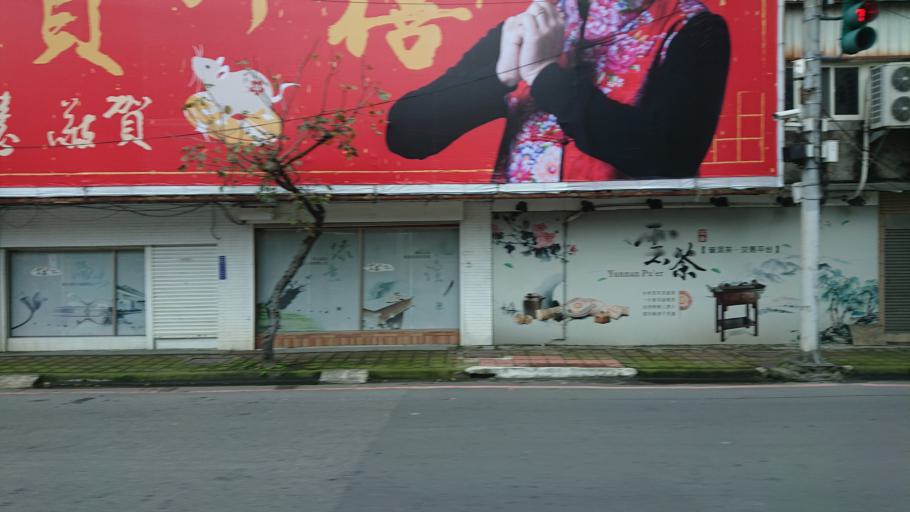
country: TW
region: Taiwan
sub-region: Taoyuan
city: Taoyuan
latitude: 24.9570
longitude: 121.3531
